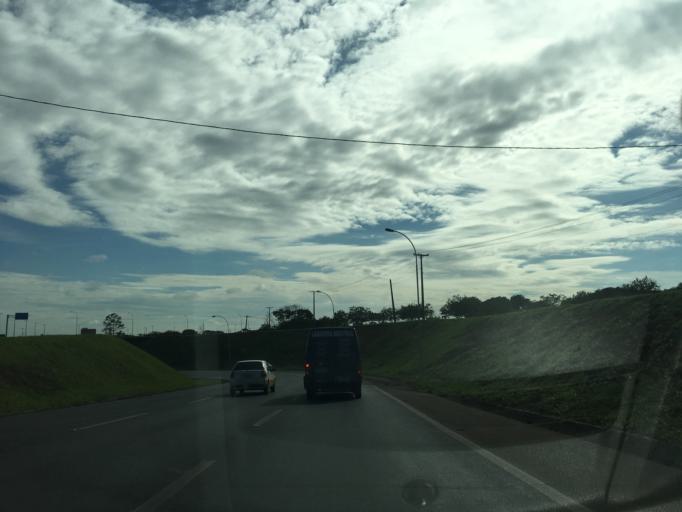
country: BR
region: Federal District
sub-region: Brasilia
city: Brasilia
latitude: -15.8643
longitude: -47.9395
